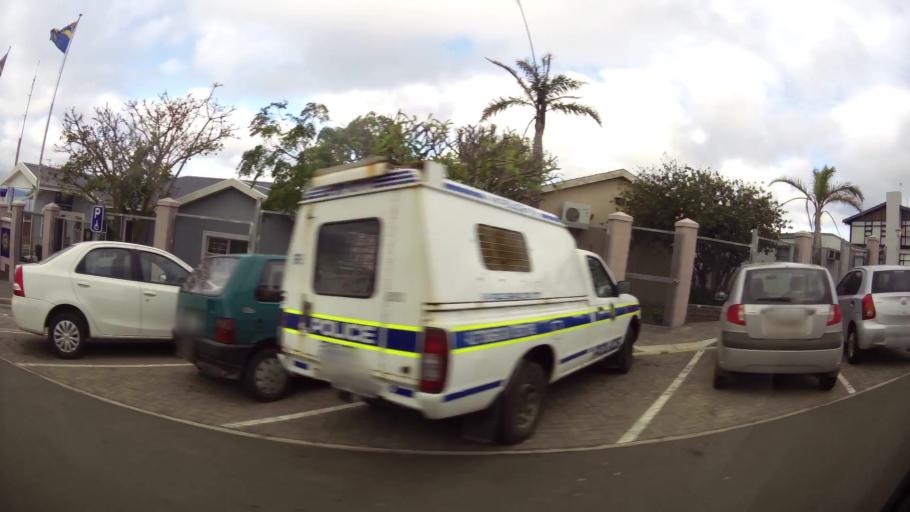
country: ZA
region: Western Cape
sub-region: Eden District Municipality
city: Plettenberg Bay
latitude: -34.0577
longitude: 23.3717
